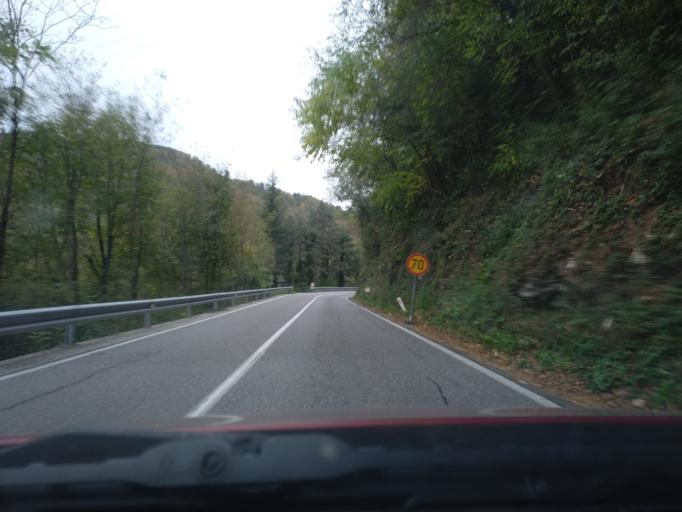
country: SI
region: Kanal
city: Kanal
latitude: 46.1142
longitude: 13.6859
